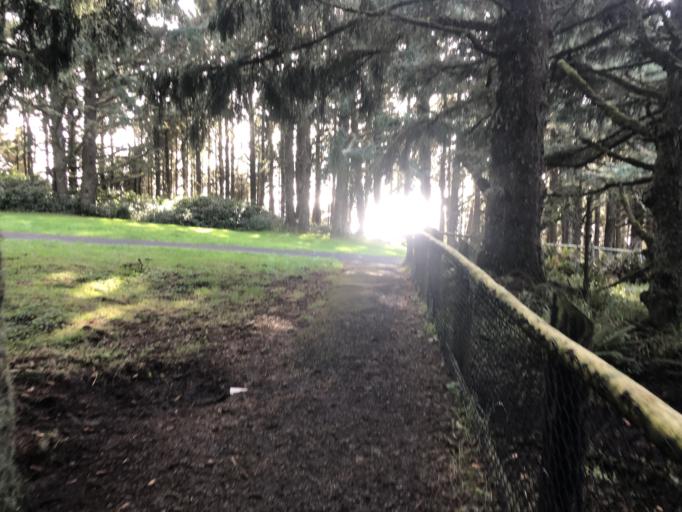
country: US
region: Oregon
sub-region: Tillamook County
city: Bay City
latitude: 45.4862
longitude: -123.9750
